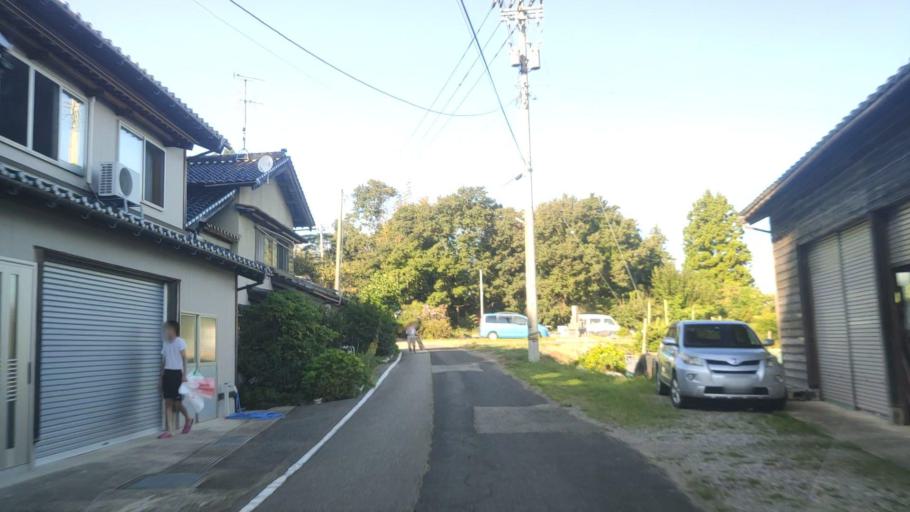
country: JP
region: Ishikawa
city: Nanao
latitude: 37.1193
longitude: 136.8938
